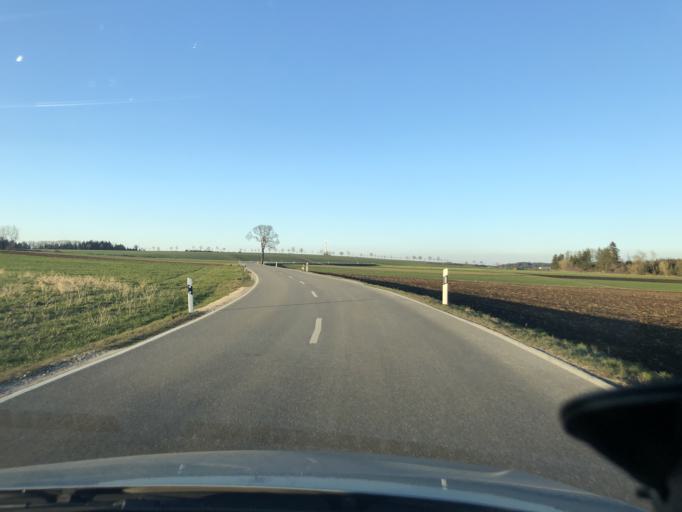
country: DE
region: Baden-Wuerttemberg
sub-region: Freiburg Region
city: Hufingen
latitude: 47.8807
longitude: 8.4727
